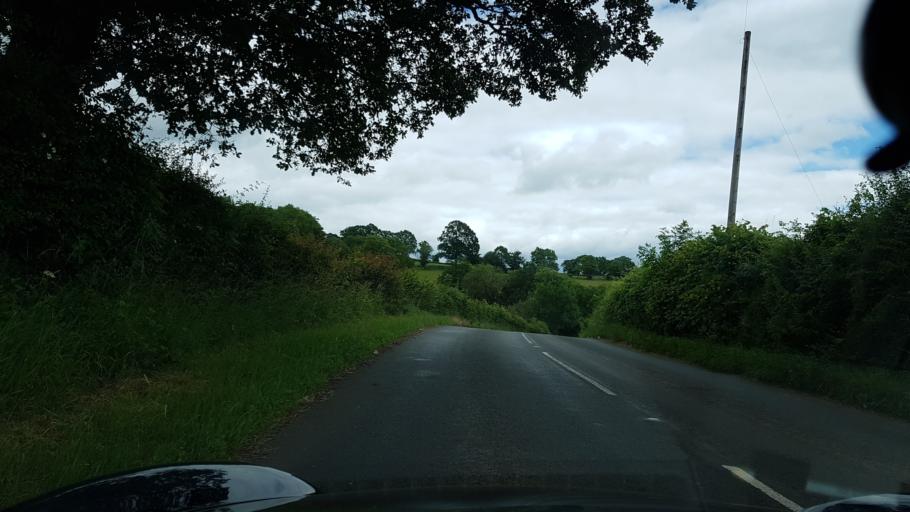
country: GB
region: Wales
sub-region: Monmouthshire
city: Grosmont
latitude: 51.8733
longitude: -2.8552
